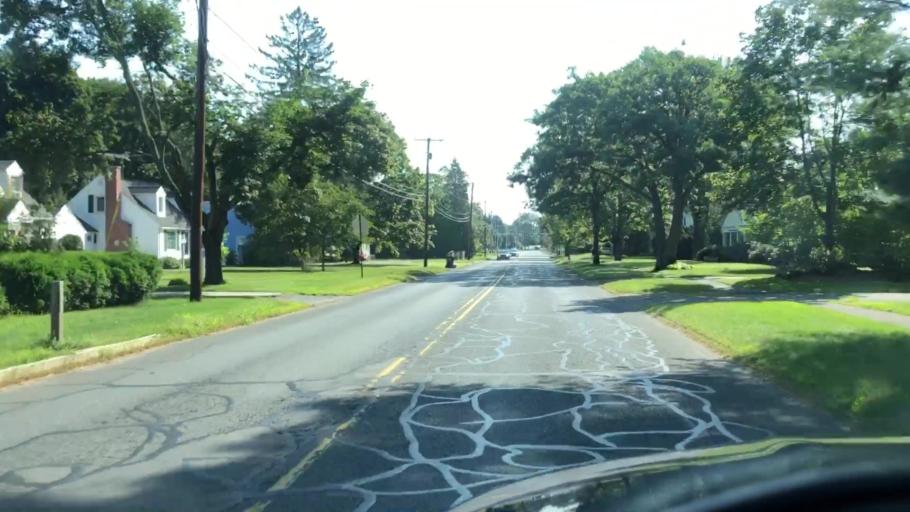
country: US
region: Massachusetts
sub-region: Hampshire County
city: Northampton
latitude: 42.3442
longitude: -72.6750
